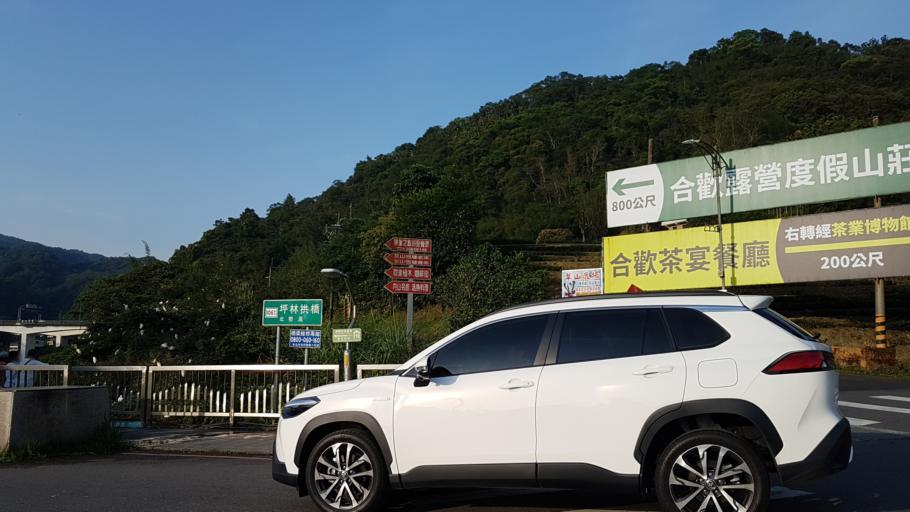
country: TW
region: Taiwan
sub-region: Yilan
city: Yilan
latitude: 24.9355
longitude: 121.7130
